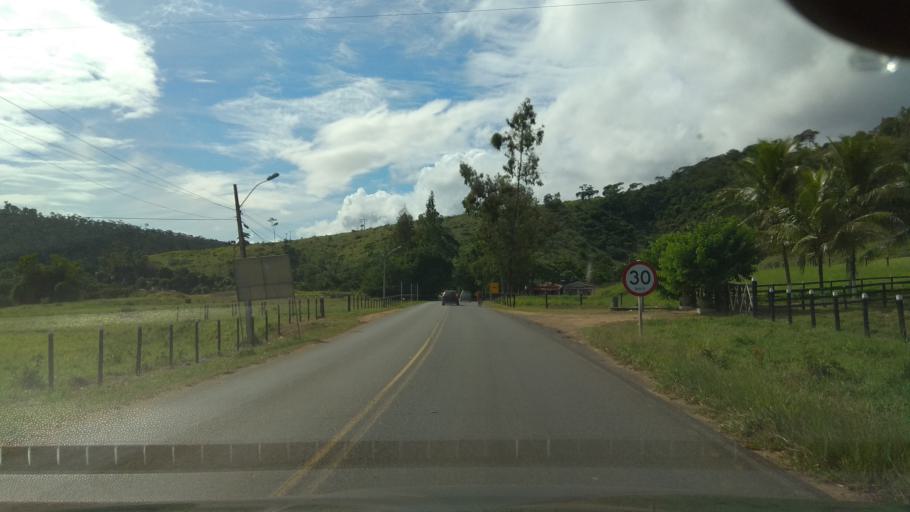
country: BR
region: Bahia
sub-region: Ubaira
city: Ubaira
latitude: -13.2719
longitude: -39.6340
